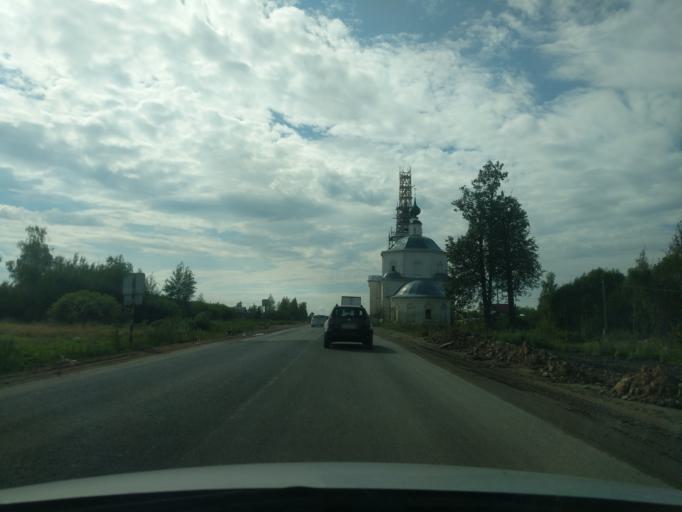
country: RU
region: Kostroma
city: Sudislavl'
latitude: 57.8631
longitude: 41.6222
